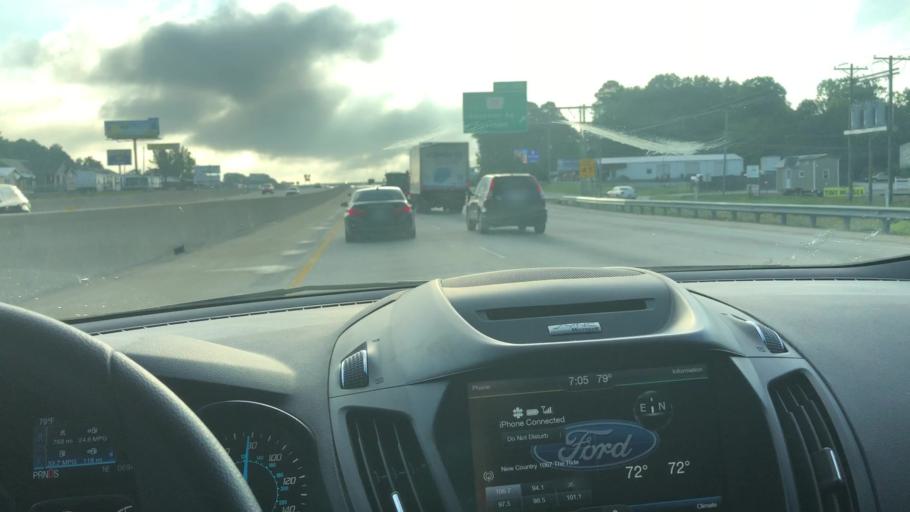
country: US
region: Arkansas
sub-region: Pulaski County
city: Alexander
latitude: 34.6379
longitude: -92.4517
